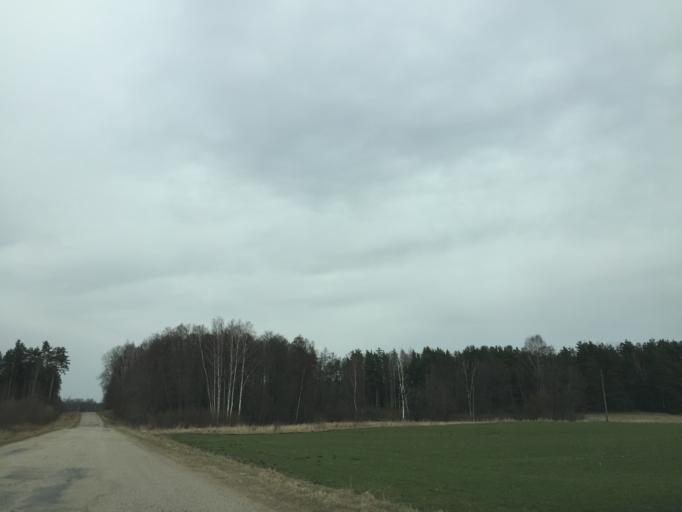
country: LV
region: Ilukste
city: Ilukste
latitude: 56.0376
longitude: 26.2773
